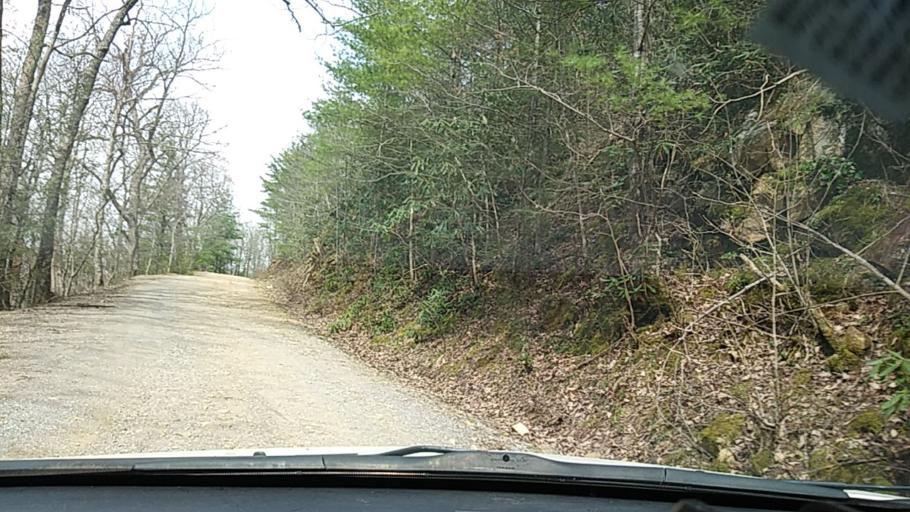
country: US
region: Tennessee
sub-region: Greene County
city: Tusculum
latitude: 36.0856
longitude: -82.6895
